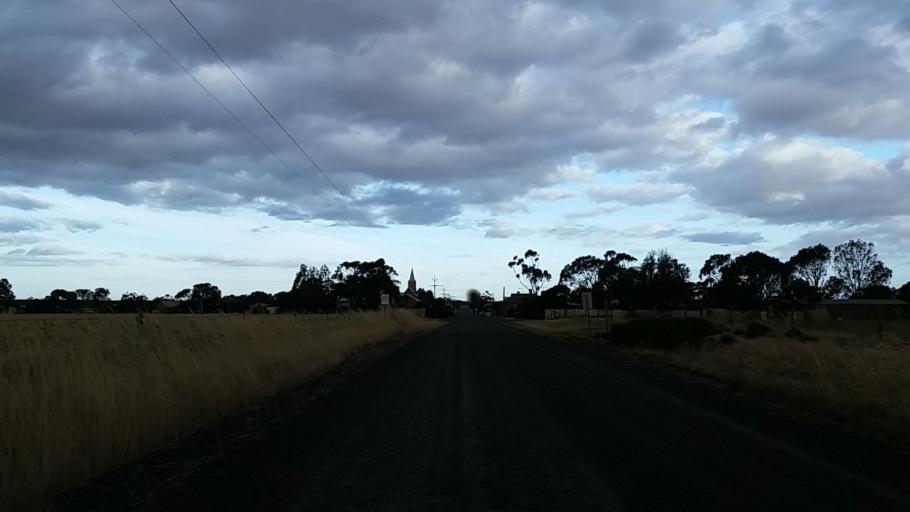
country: AU
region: South Australia
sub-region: Barossa
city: Angaston
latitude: -34.5729
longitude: 139.2906
